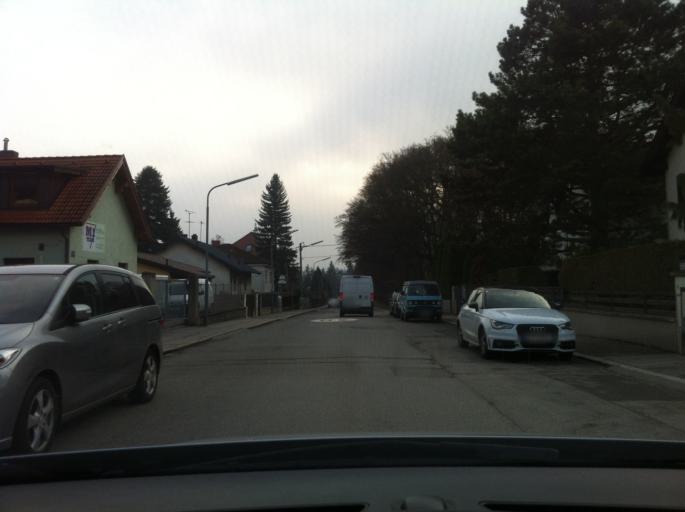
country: AT
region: Lower Austria
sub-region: Politischer Bezirk Wien-Umgebung
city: Purkersdorf
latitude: 48.2224
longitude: 16.2472
